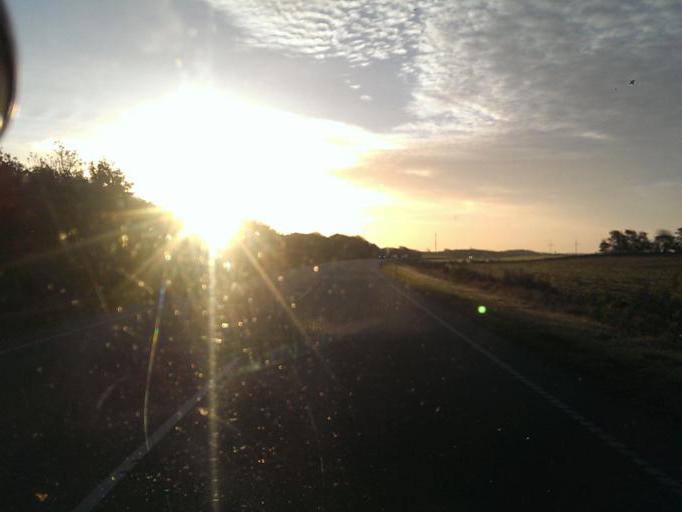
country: DK
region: South Denmark
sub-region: Esbjerg Kommune
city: Bramming
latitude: 55.4752
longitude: 8.6582
